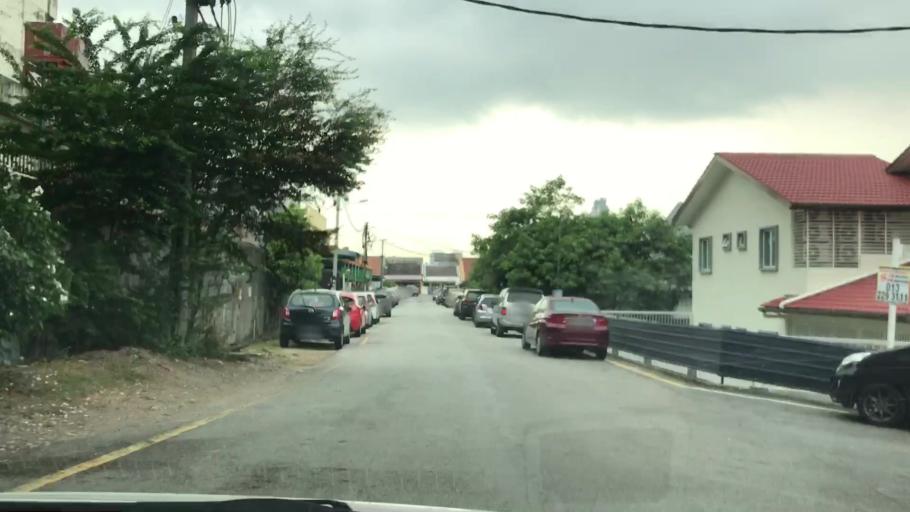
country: MY
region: Selangor
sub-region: Petaling
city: Petaling Jaya
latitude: 3.1083
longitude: 101.6216
